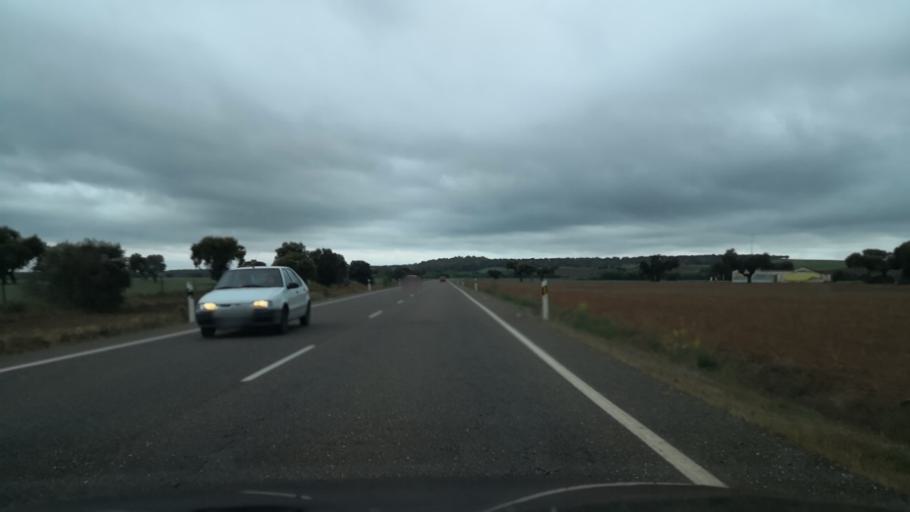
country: ES
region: Extremadura
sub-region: Provincia de Badajoz
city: La Roca de la Sierra
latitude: 39.0619
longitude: -6.7667
